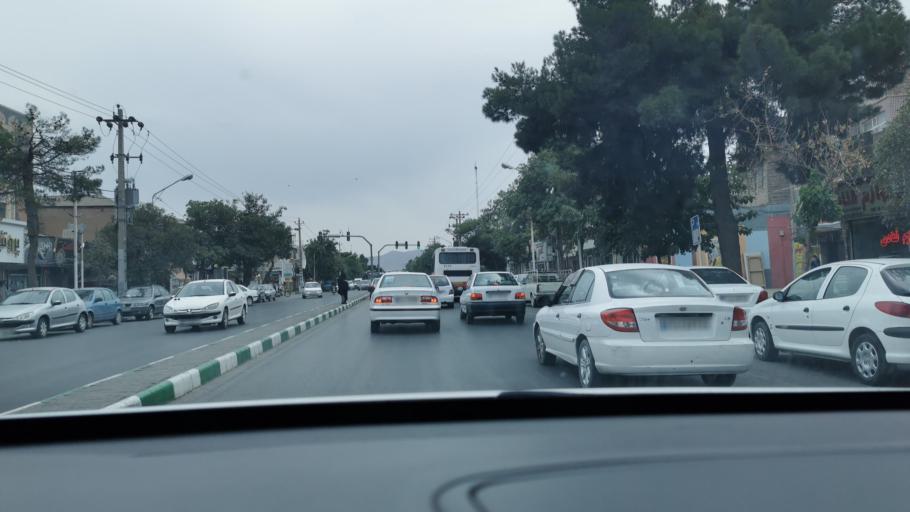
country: IR
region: Razavi Khorasan
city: Mashhad
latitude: 36.3183
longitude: 59.6185
